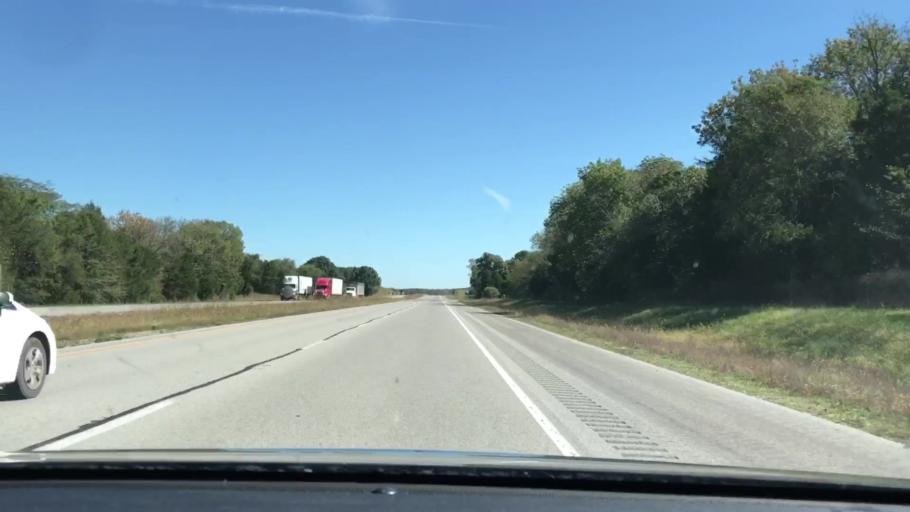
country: US
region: Kentucky
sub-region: Logan County
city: Auburn
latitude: 36.8477
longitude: -86.7802
